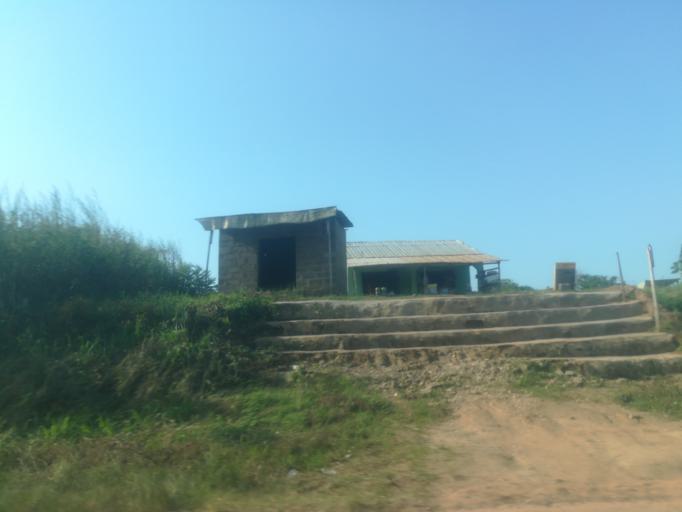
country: NG
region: Ogun
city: Abeokuta
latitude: 7.1407
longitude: 3.2513
